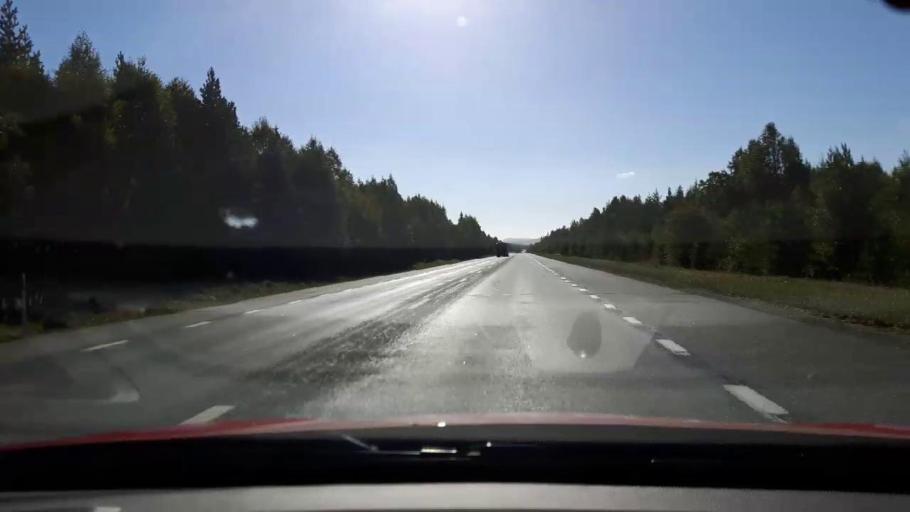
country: SE
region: Vaesternorrland
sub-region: Ange Kommun
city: Ange
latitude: 62.5932
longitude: 15.7097
